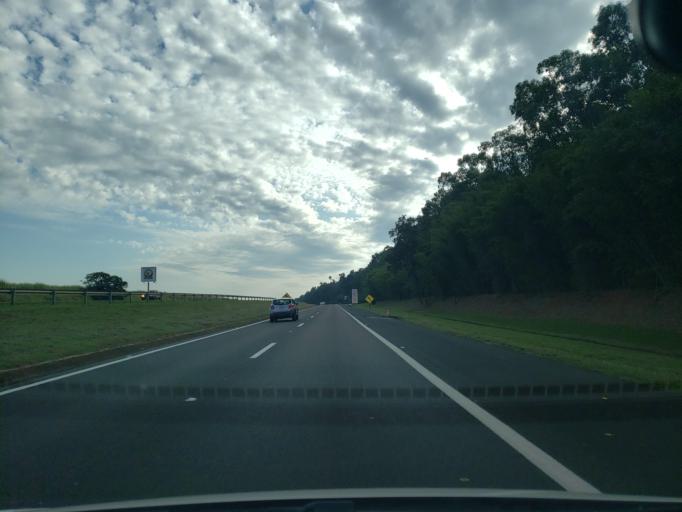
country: BR
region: Sao Paulo
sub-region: Guararapes
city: Guararapes
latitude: -21.1999
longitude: -50.5633
